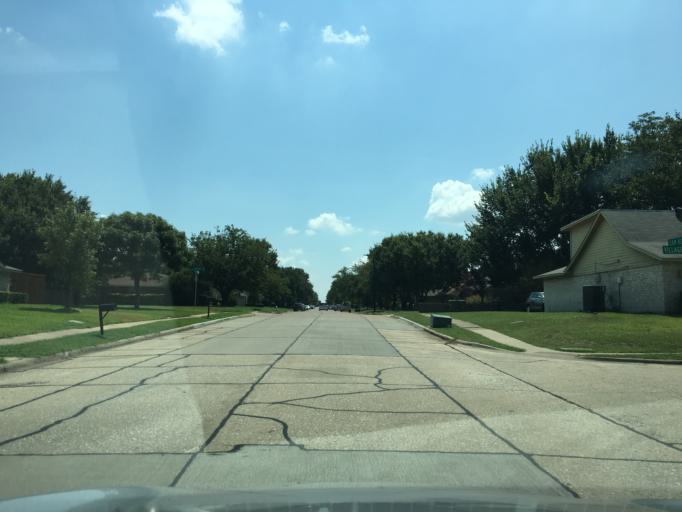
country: US
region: Texas
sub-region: Dallas County
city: Garland
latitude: 32.9421
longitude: -96.6570
